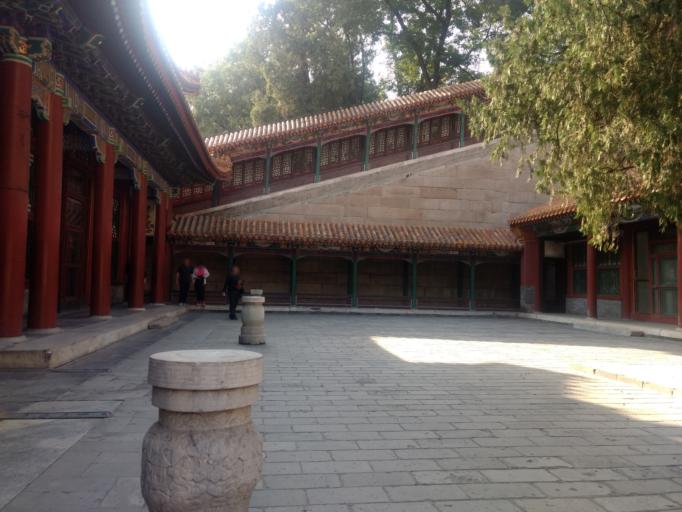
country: CN
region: Beijing
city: Haidian
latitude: 39.9973
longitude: 116.2679
